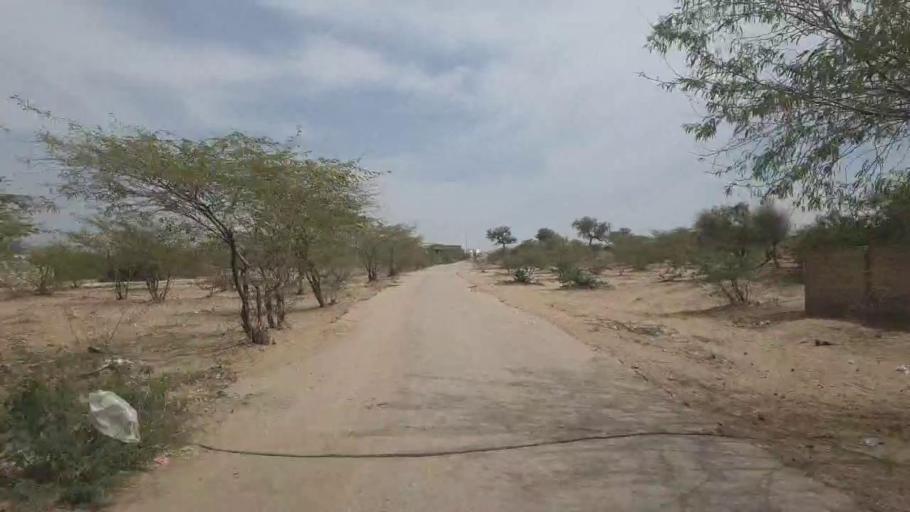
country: PK
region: Sindh
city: Umarkot
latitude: 25.2219
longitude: 69.7174
